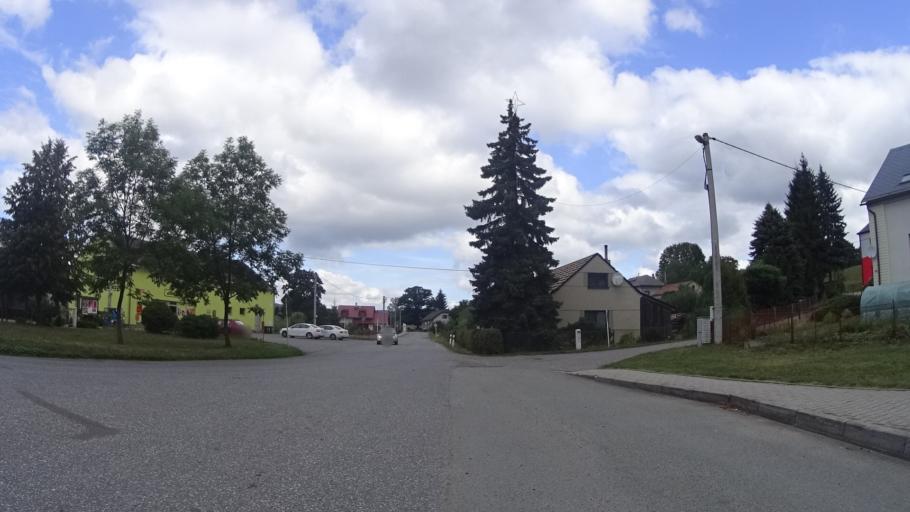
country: CZ
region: Pardubicky
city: Dolni Cermna
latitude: 49.9287
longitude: 16.5426
